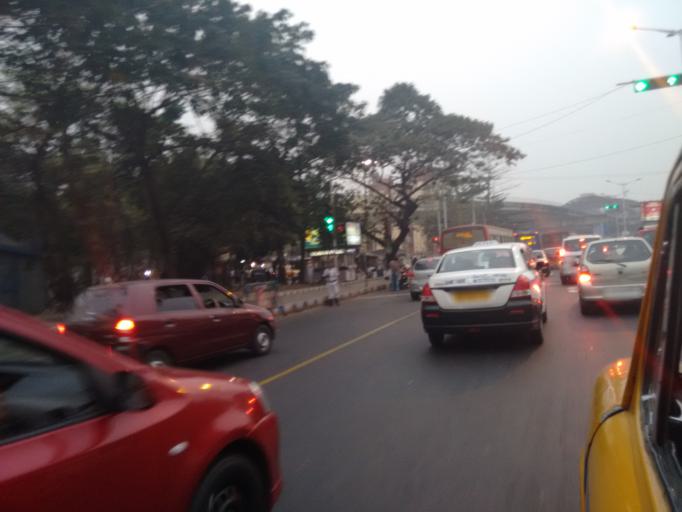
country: IN
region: West Bengal
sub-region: Kolkata
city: Kolkata
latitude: 22.5705
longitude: 88.4041
